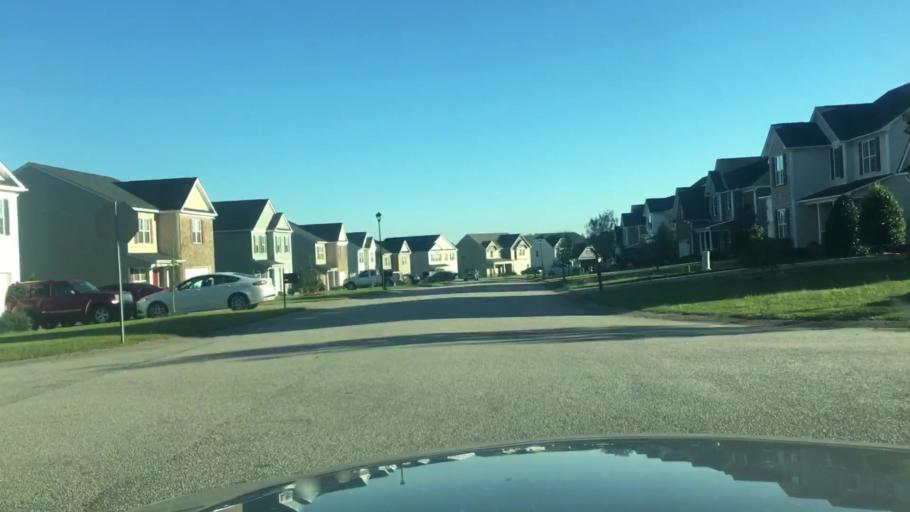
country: US
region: North Carolina
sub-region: Harnett County
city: Lillington
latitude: 35.3460
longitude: -78.8510
